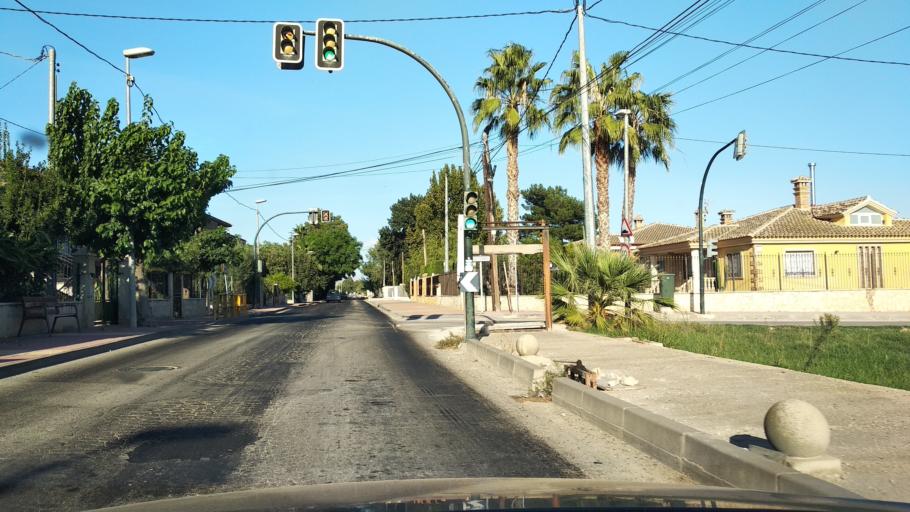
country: ES
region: Murcia
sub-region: Murcia
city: Santomera
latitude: 38.0452
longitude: -1.0375
